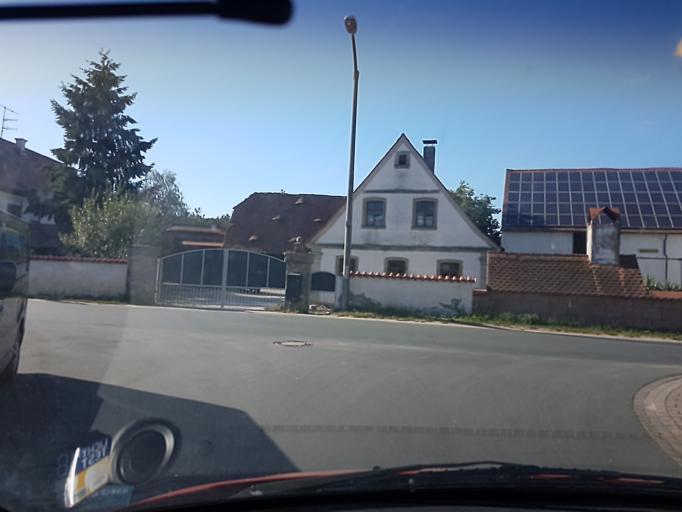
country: DE
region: Bavaria
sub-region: Upper Franconia
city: Hallerndorf
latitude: 49.7332
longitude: 10.9402
